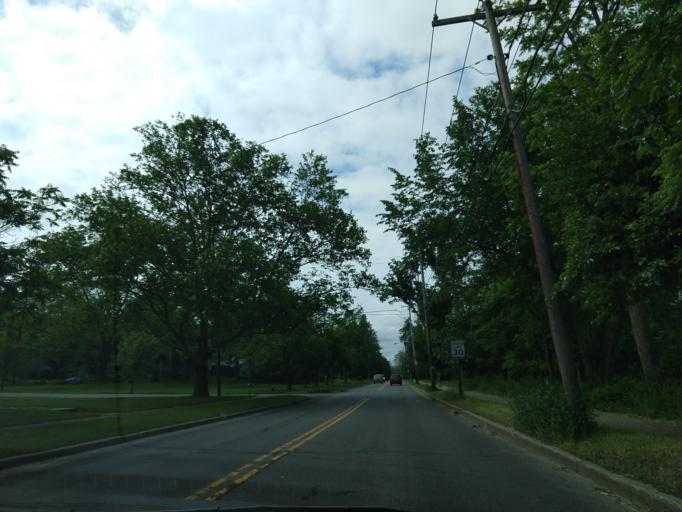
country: US
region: New York
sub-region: Erie County
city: East Aurora
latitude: 42.7622
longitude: -78.6080
